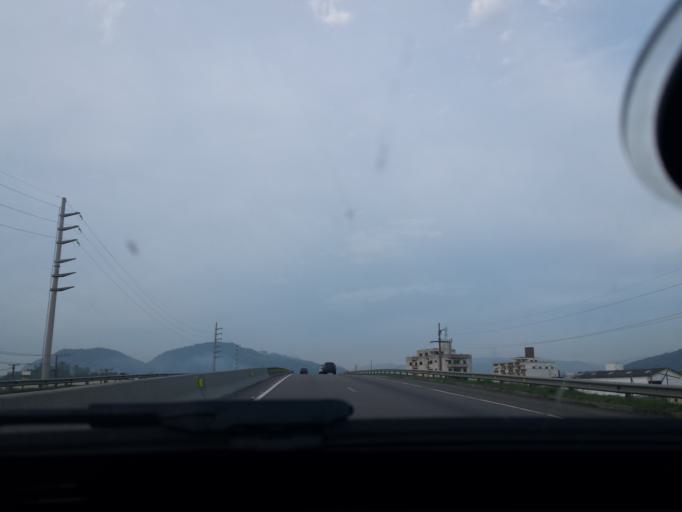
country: BR
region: Santa Catarina
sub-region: Tubarao
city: Tubarao
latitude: -28.4690
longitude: -49.0136
